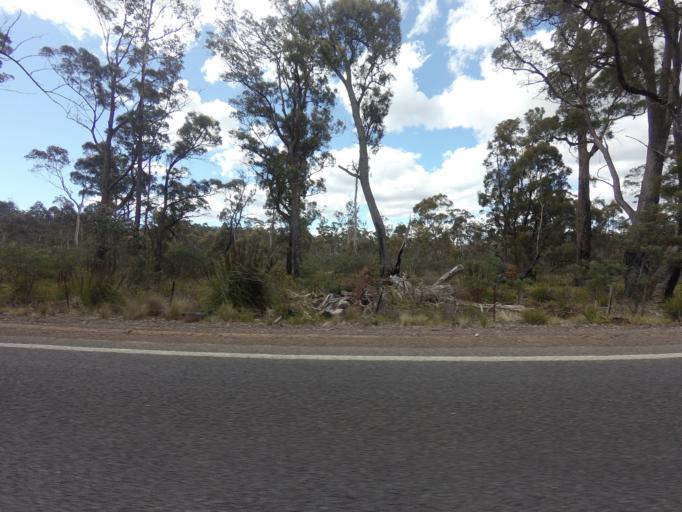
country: AU
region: Tasmania
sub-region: Northern Midlands
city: Evandale
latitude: -41.9650
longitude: 147.6373
